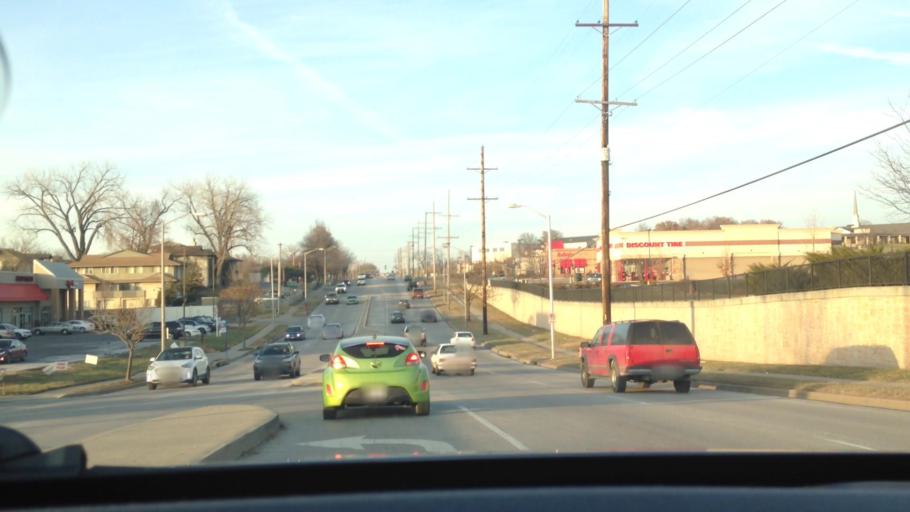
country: US
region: Missouri
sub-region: Clay County
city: Gladstone
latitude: 39.1822
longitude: -94.5766
